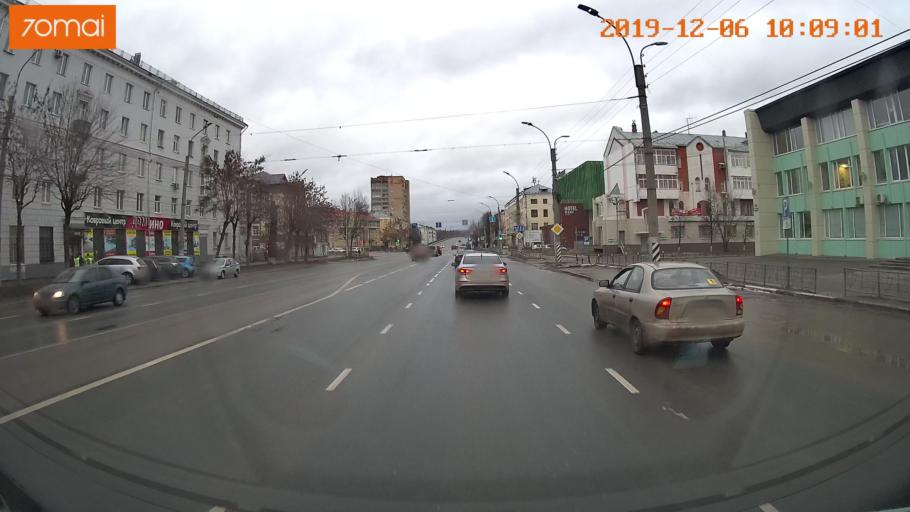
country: RU
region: Ivanovo
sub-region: Gorod Ivanovo
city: Ivanovo
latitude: 57.0199
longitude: 40.9686
